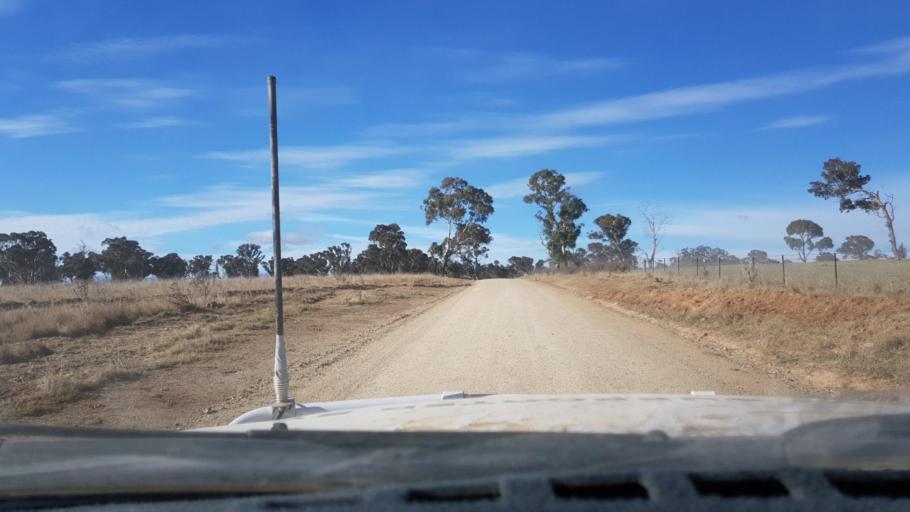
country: AU
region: New South Wales
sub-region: Armidale Dumaresq
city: Enmore
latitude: -30.7092
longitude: 151.5890
